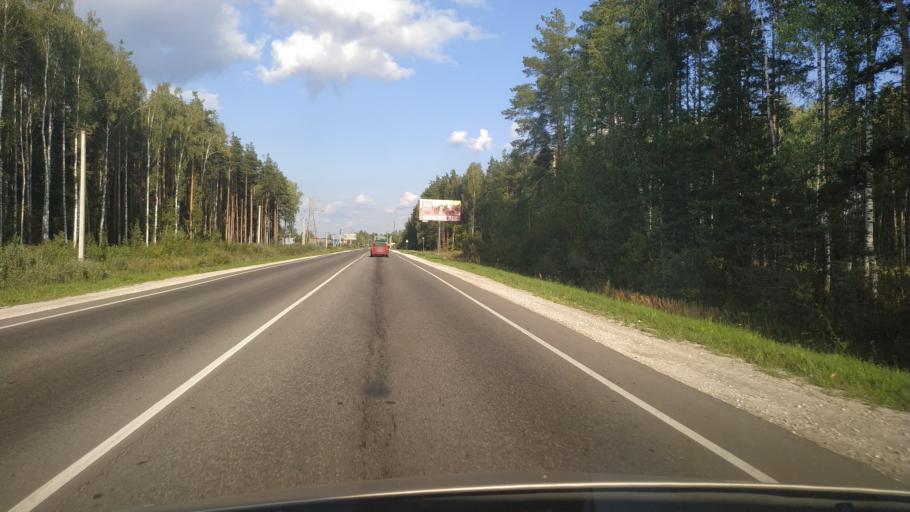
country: RU
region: Moskovskaya
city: Shaturtorf
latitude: 55.5790
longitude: 39.4554
